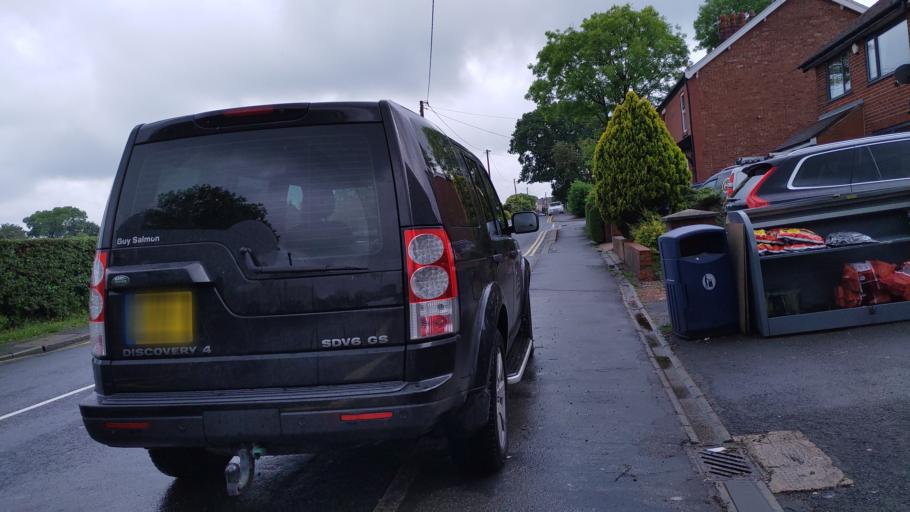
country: GB
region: England
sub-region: Lancashire
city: Coppull
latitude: 53.6292
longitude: -2.7097
